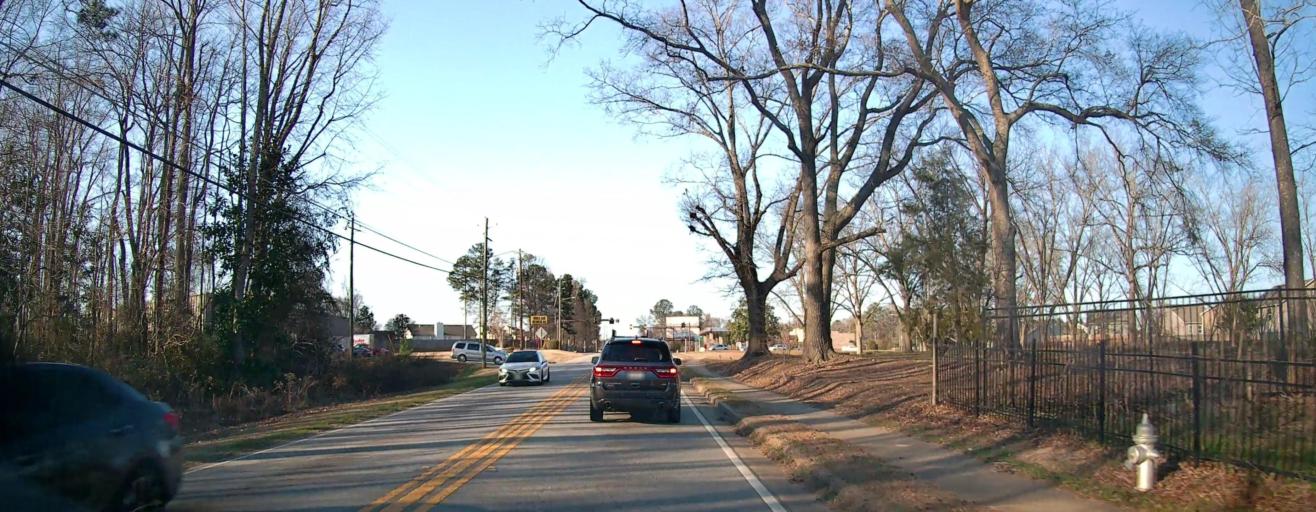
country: US
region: Georgia
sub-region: Clayton County
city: Lovejoy
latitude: 33.4403
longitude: -84.3151
